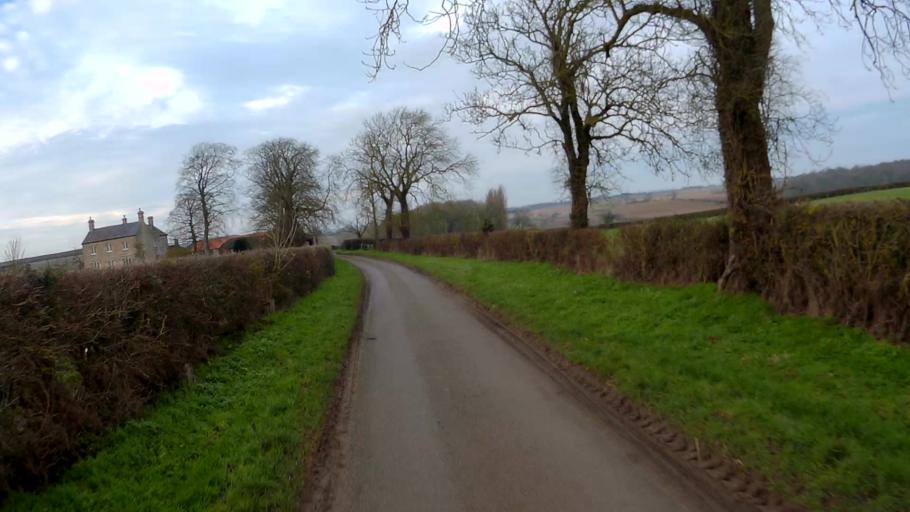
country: GB
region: England
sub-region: Lincolnshire
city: Bourne
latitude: 52.8233
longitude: -0.4584
